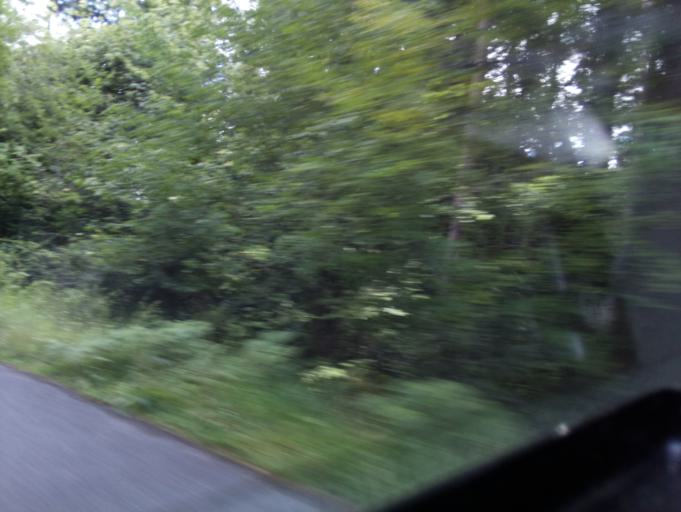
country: GB
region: England
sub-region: Gloucestershire
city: Cinderford
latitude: 51.7986
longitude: -2.4934
